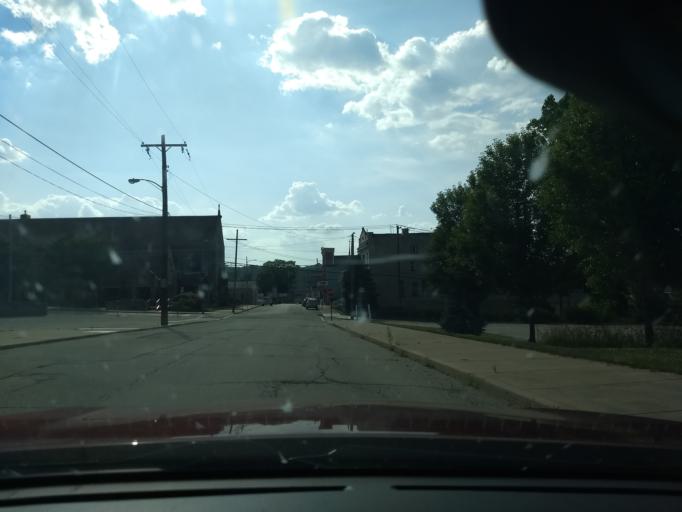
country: US
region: Pennsylvania
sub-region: Westmoreland County
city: Irwin
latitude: 40.3333
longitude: -79.7083
